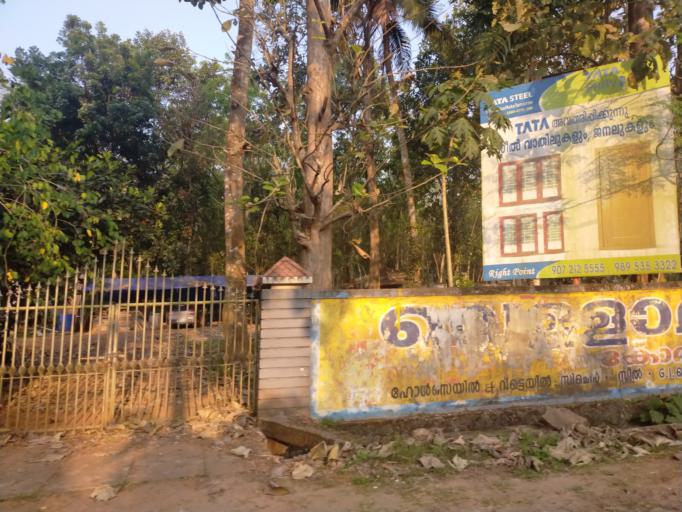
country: IN
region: Kerala
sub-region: Kottayam
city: Vaikam
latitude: 9.7493
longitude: 76.5080
